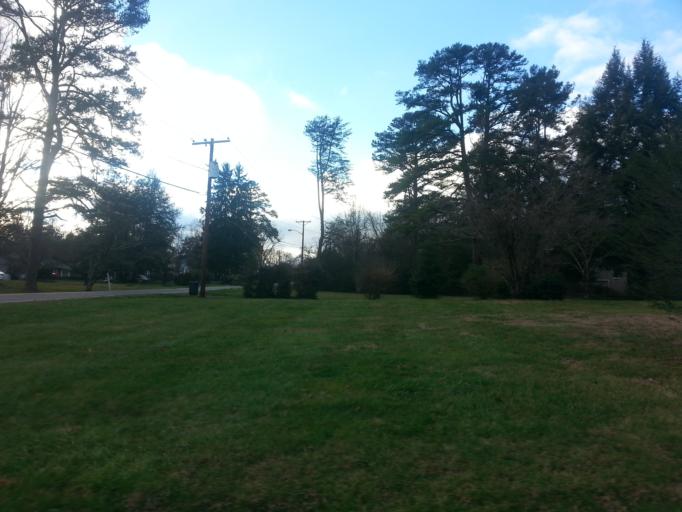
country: US
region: Tennessee
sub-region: Knox County
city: Knoxville
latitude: 36.0015
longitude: -83.8504
